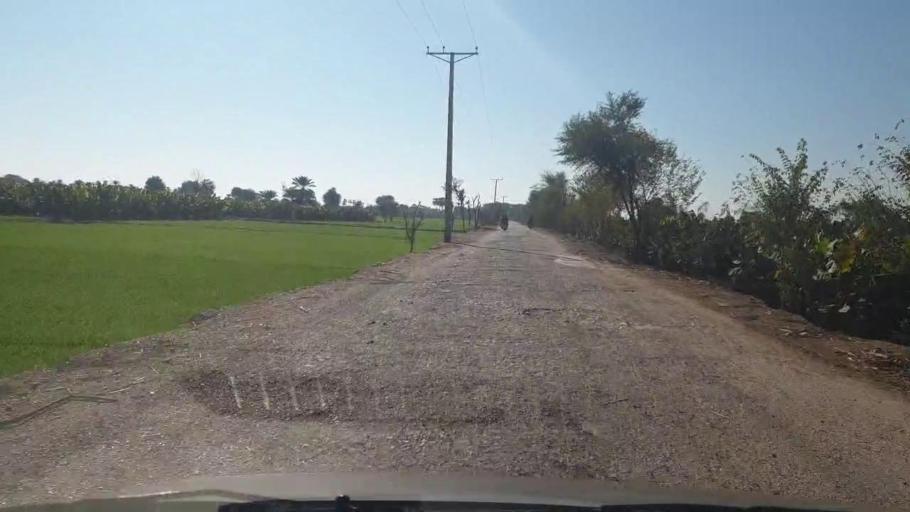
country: PK
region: Sindh
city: Bozdar
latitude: 27.2537
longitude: 68.6522
